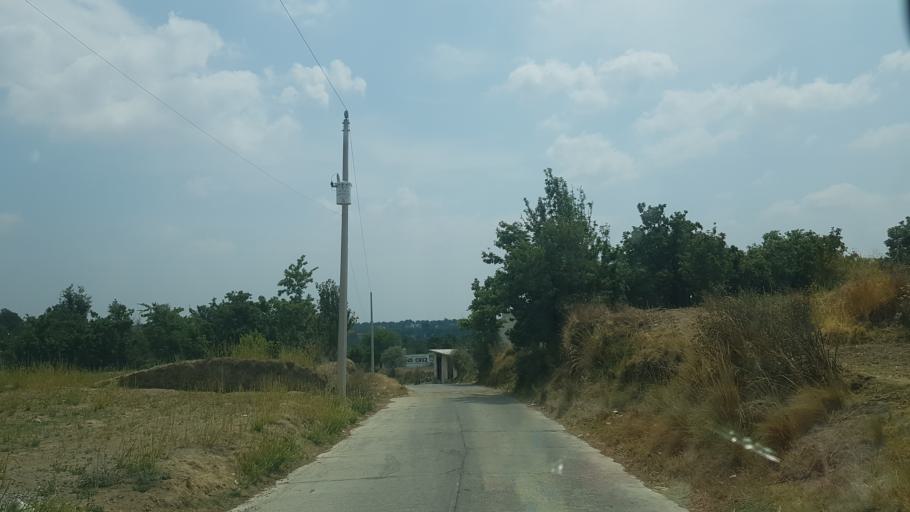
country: MX
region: Puebla
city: Domingo Arenas
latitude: 19.1377
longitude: -98.4801
